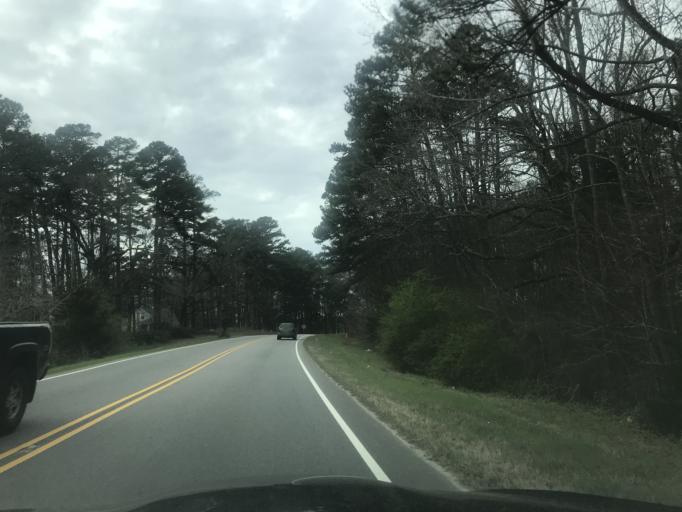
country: US
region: North Carolina
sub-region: Franklin County
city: Franklinton
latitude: 36.0944
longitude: -78.4132
